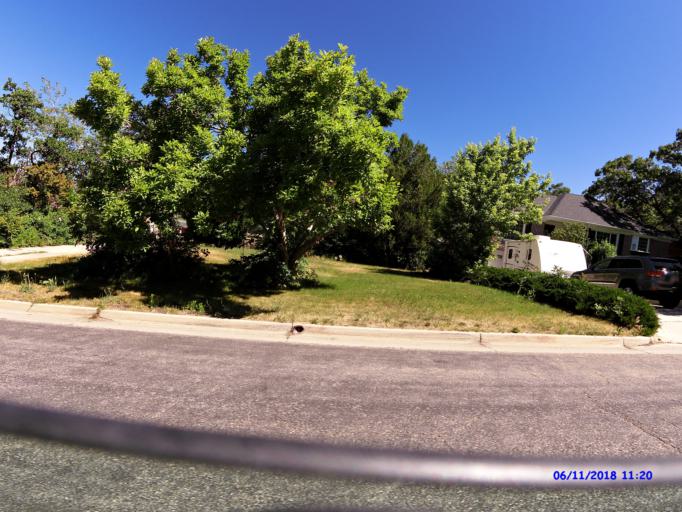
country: US
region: Utah
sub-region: Weber County
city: Ogden
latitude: 41.2223
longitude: -111.9338
